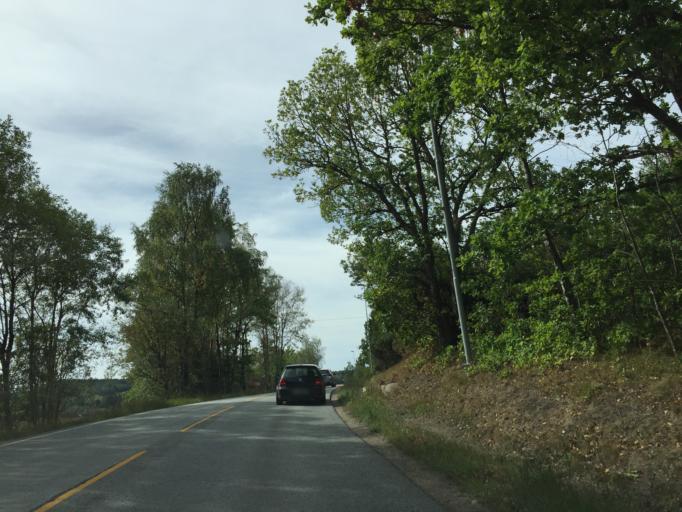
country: NO
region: Ostfold
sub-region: Fredrikstad
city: Fredrikstad
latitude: 59.2647
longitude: 10.8959
